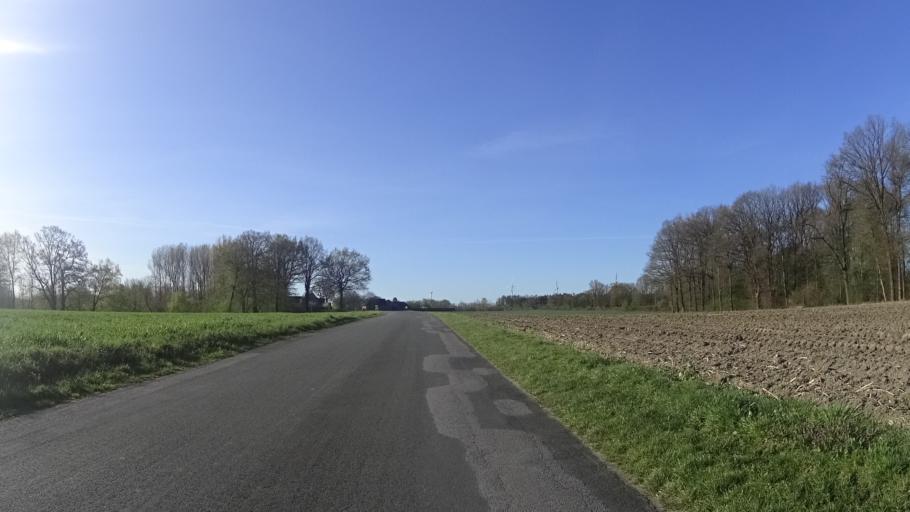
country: DE
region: North Rhine-Westphalia
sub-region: Regierungsbezirk Munster
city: Greven
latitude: 52.0728
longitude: 7.6083
